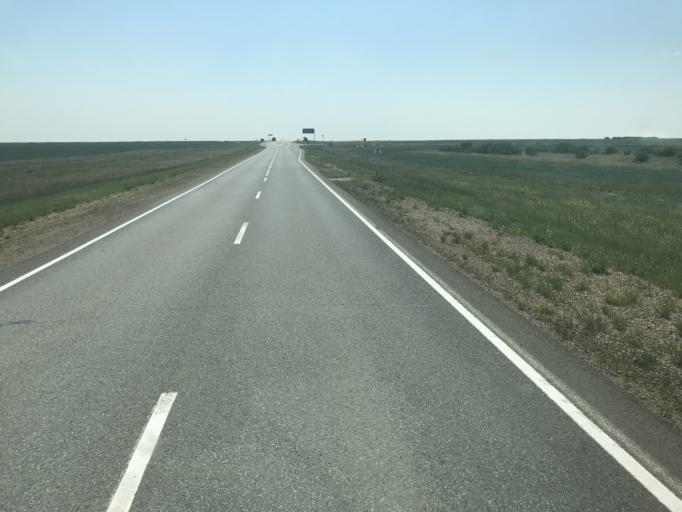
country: KZ
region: Soltustik Qazaqstan
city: Taiynsha
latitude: 53.9634
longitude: 69.2100
